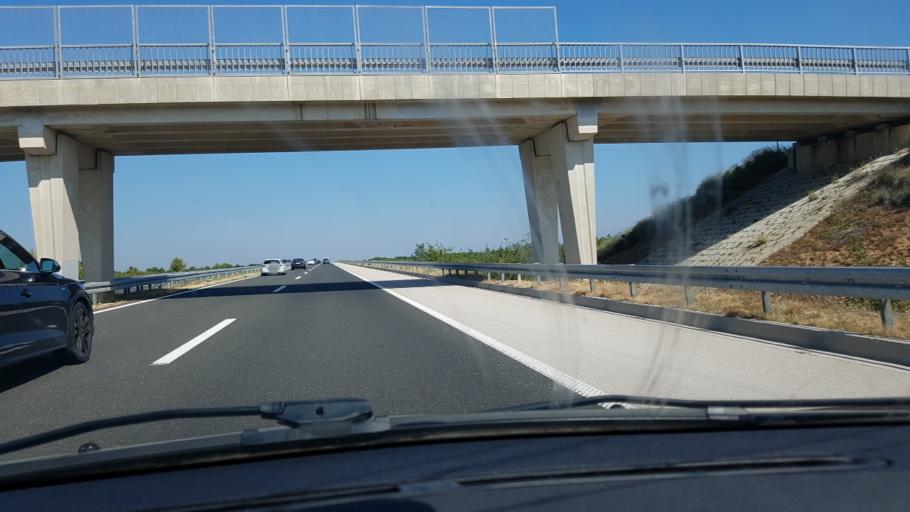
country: HR
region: Zadarska
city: Benkovac
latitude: 43.9740
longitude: 15.6446
